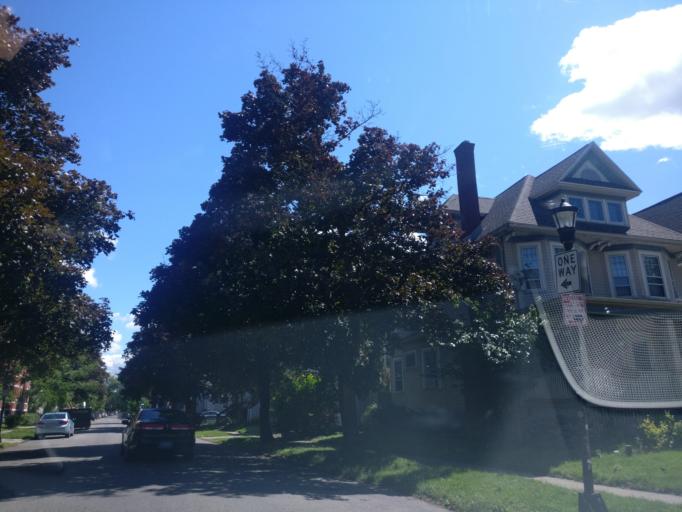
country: US
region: New York
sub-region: Erie County
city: Buffalo
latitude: 42.9261
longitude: -78.8809
